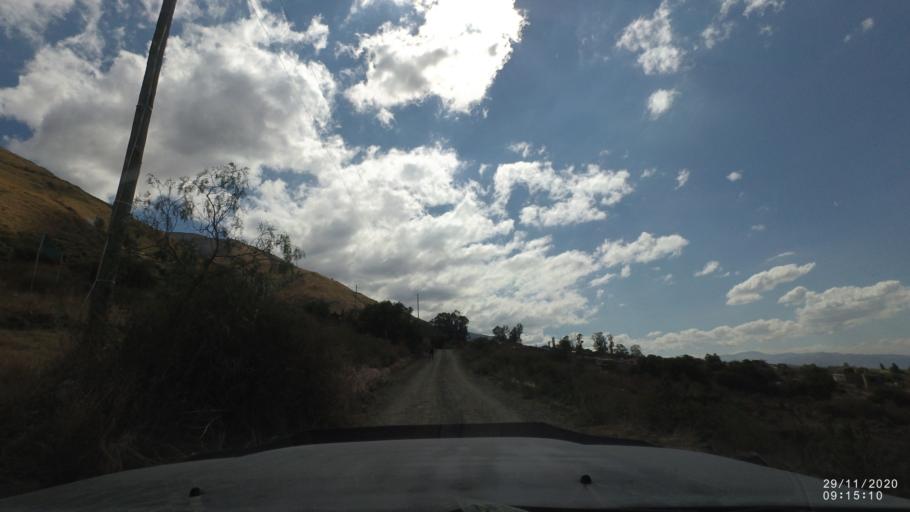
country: BO
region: Cochabamba
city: Cochabamba
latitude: -17.3268
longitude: -66.1908
